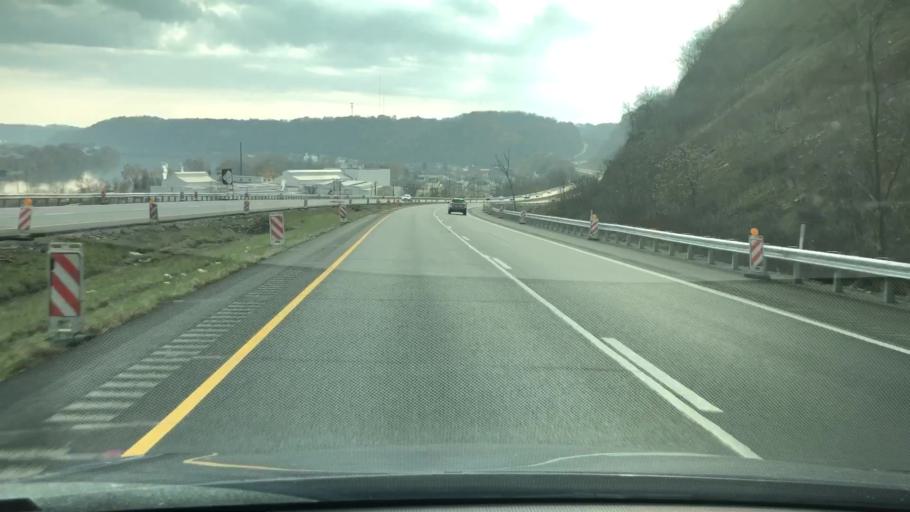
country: US
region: Pennsylvania
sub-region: Allegheny County
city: Tarentum
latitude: 40.5937
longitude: -79.7718
